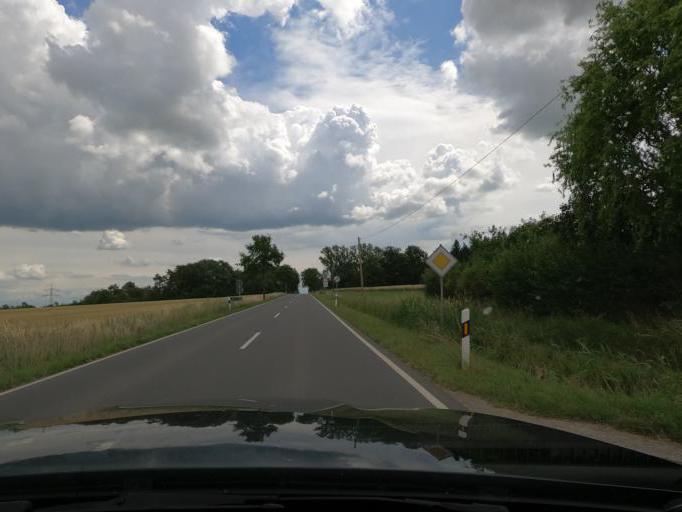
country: DE
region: Lower Saxony
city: Sehnde
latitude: 52.2963
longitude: 9.9925
